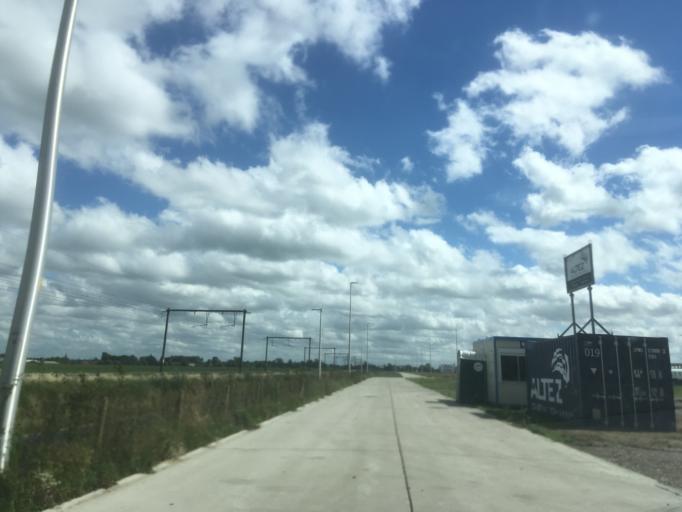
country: BE
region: Flanders
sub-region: Provincie West-Vlaanderen
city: Torhout
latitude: 51.0504
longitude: 3.1092
